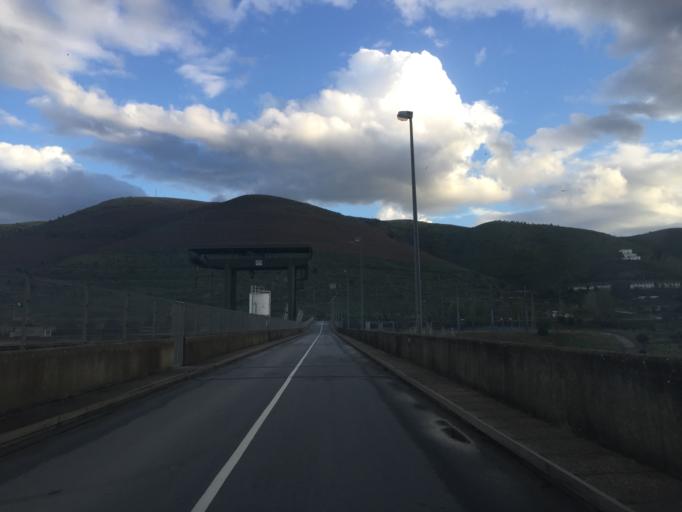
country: PT
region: Braganca
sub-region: Torre de Moncorvo
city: Torre de Moncorvo
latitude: 41.1358
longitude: -7.1145
